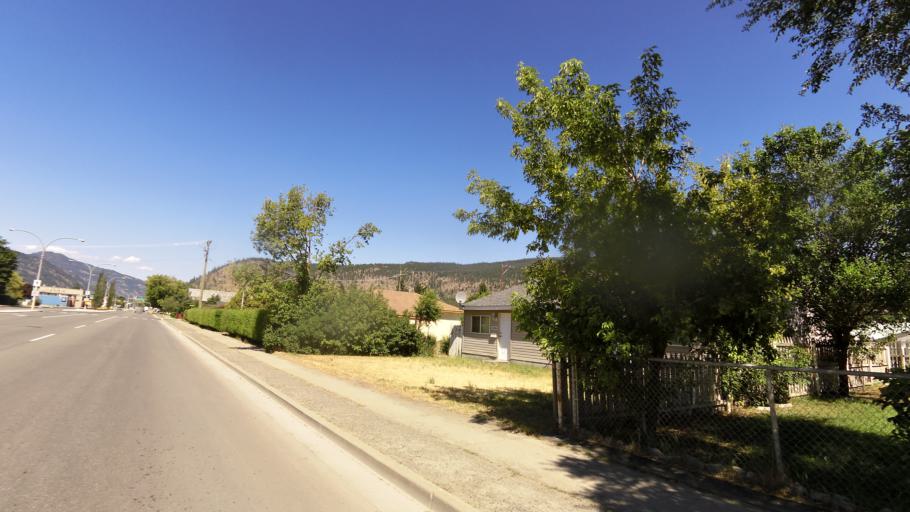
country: CA
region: British Columbia
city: Merritt
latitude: 50.1104
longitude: -120.7827
